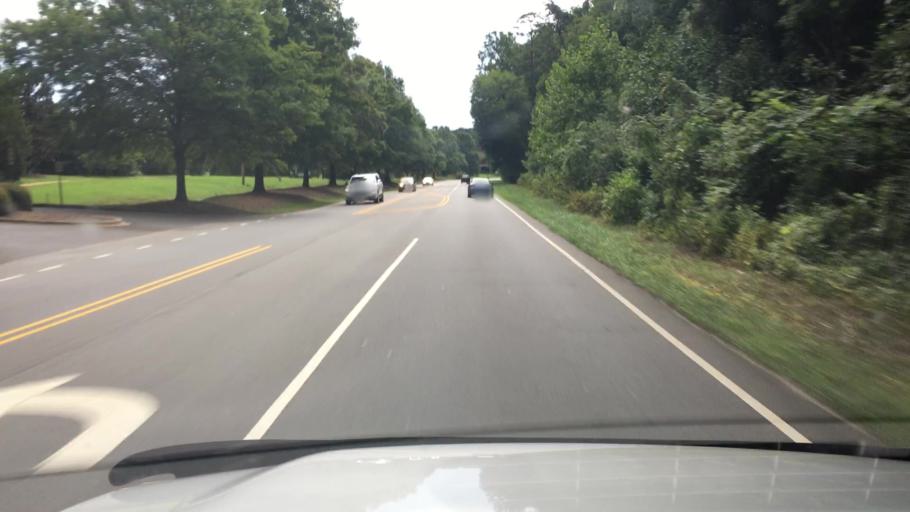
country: US
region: North Carolina
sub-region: Mecklenburg County
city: Huntersville
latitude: 35.3772
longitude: -80.9117
